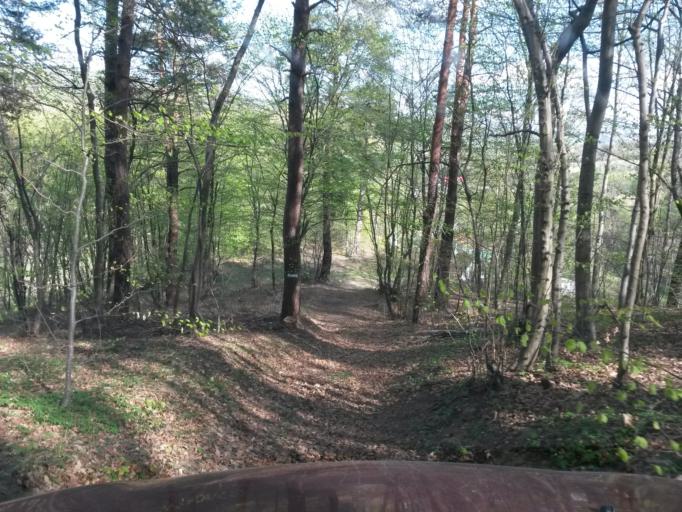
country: SK
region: Presovsky
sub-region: Okres Presov
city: Presov
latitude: 48.9471
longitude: 21.1605
